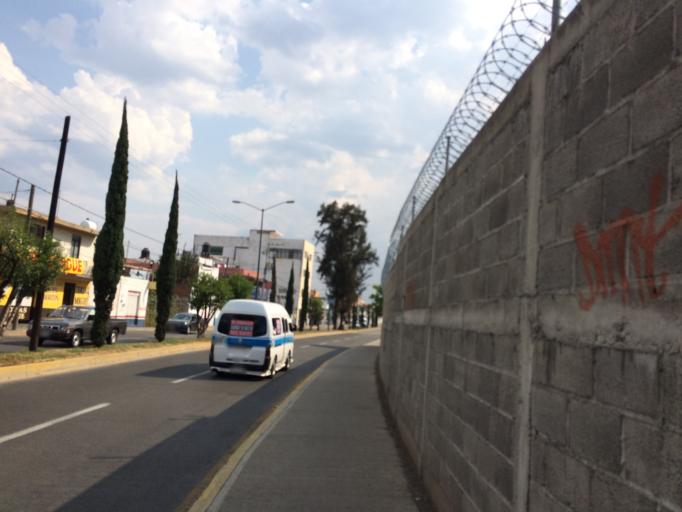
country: MX
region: Michoacan
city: Morelia
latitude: 19.6961
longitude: -101.2189
